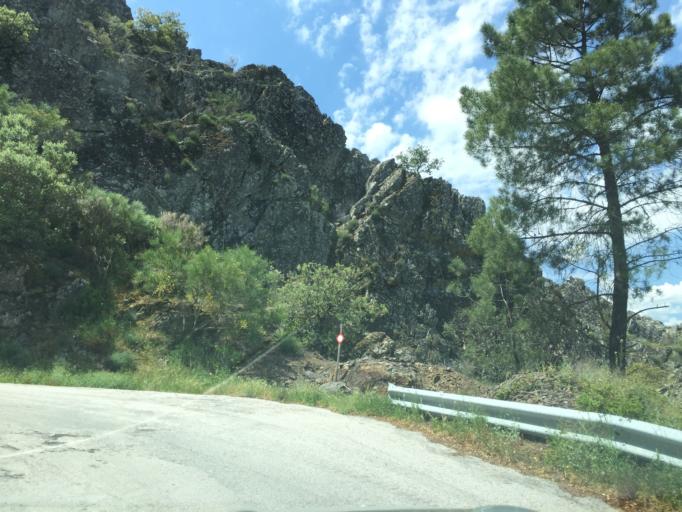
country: PT
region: Coimbra
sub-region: Pampilhosa da Serra
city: Pampilhosa da Serra
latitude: 40.0860
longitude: -7.8638
